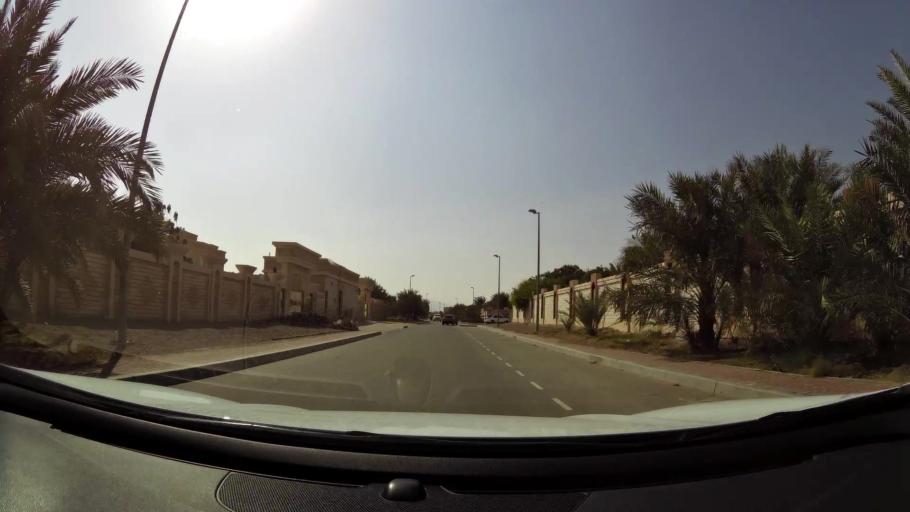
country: AE
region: Abu Dhabi
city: Al Ain
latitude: 24.1016
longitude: 55.9173
